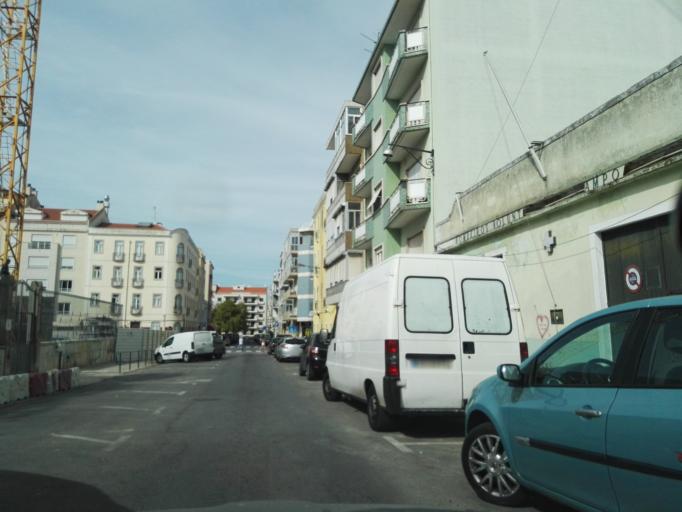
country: PT
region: Lisbon
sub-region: Lisbon
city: Lisbon
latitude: 38.7186
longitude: -9.1664
